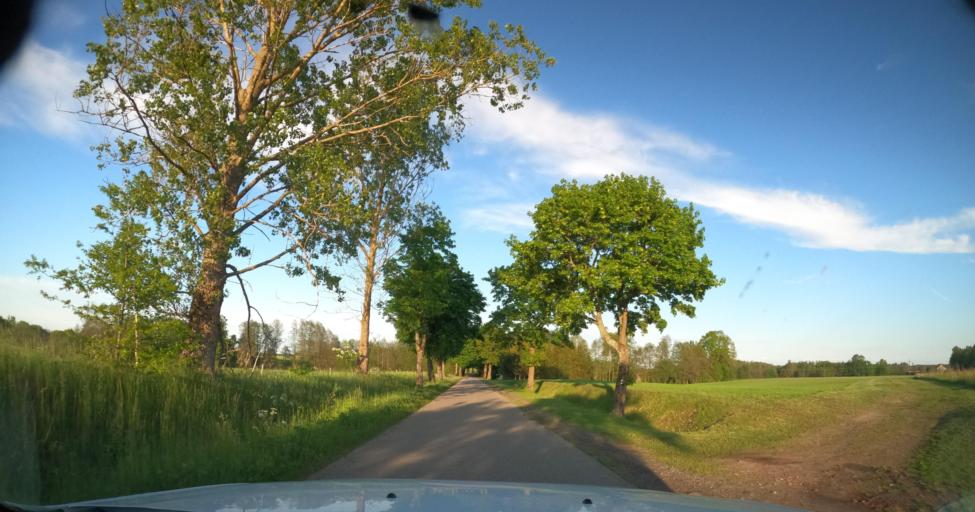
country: PL
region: Warmian-Masurian Voivodeship
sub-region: Powiat lidzbarski
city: Orneta
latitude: 54.1711
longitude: 20.1695
